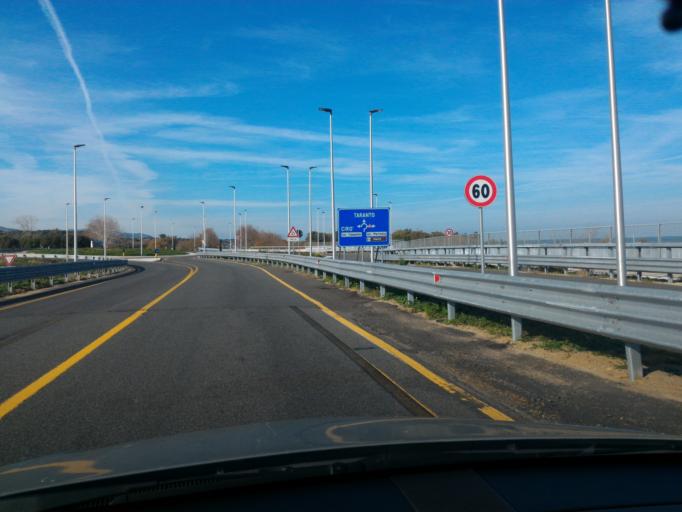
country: IT
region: Calabria
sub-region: Provincia di Crotone
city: Ciro
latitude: 39.4195
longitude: 17.0794
